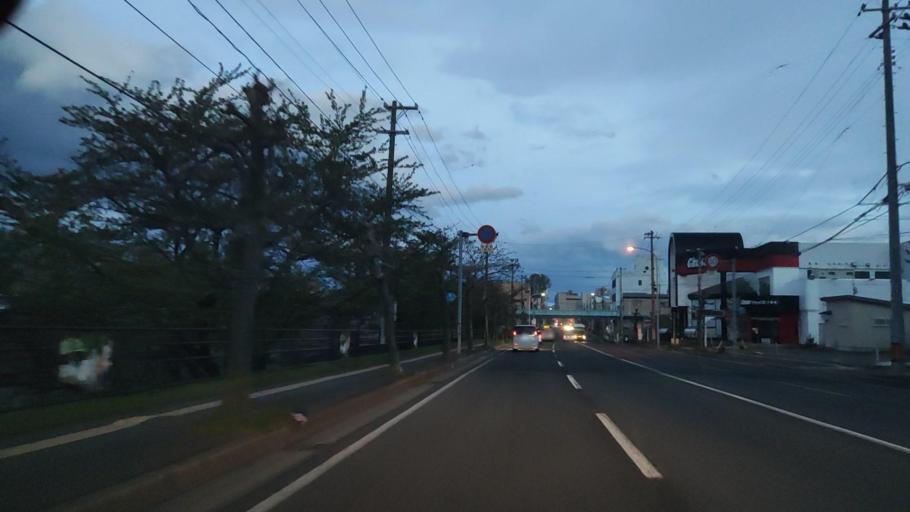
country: JP
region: Iwate
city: Morioka-shi
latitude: 39.7119
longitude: 141.1314
